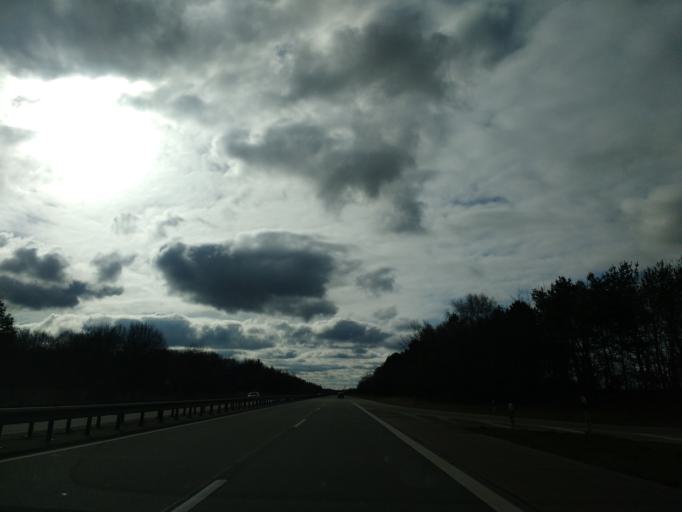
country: DE
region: Lower Saxony
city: Midlum
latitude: 53.7256
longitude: 8.6619
